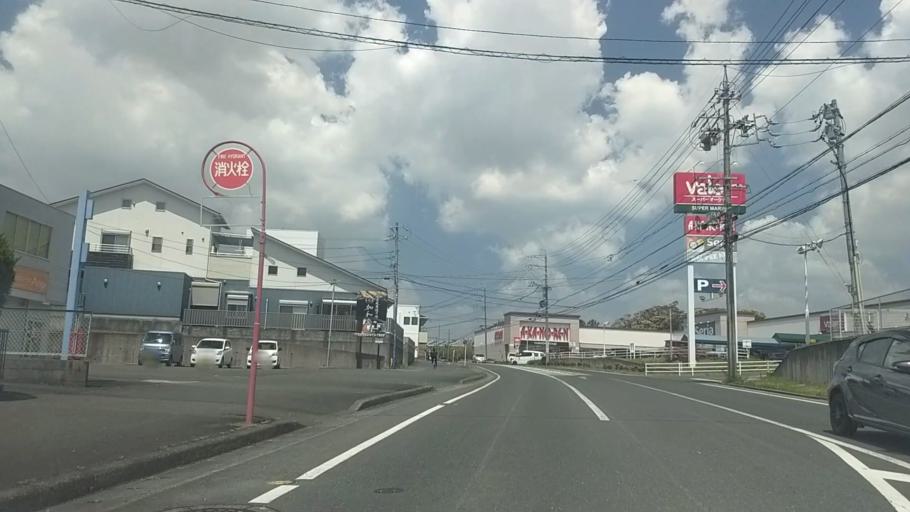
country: JP
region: Shizuoka
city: Hamamatsu
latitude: 34.7524
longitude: 137.7351
